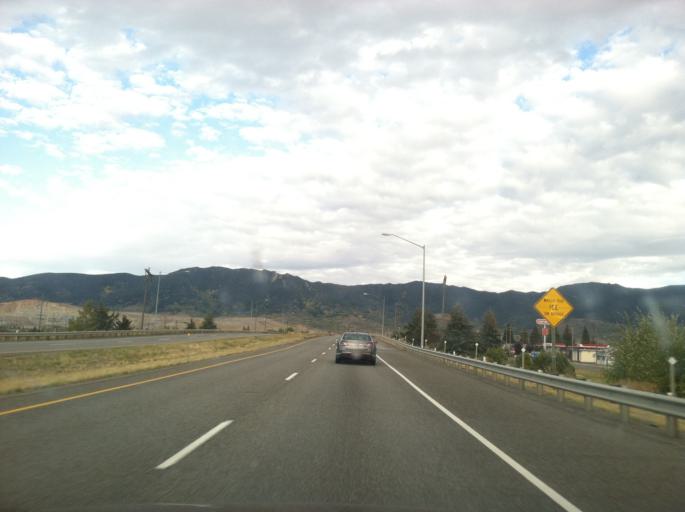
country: US
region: Montana
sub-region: Silver Bow County
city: Butte
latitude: 45.9924
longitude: -112.5423
